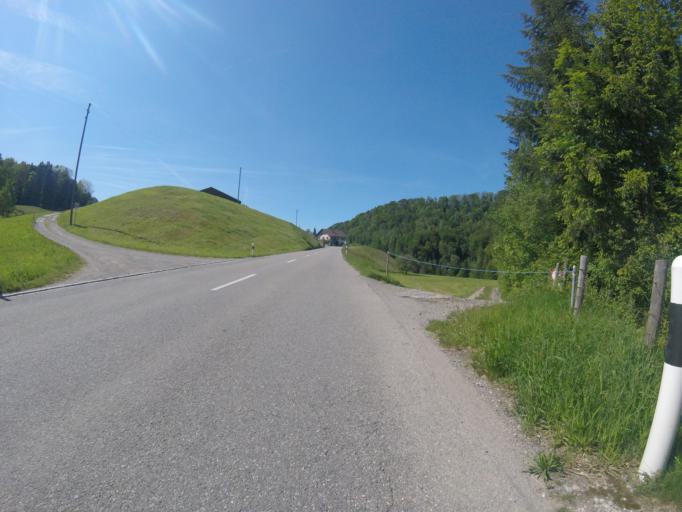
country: CH
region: Saint Gallen
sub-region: Wahlkreis Toggenburg
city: Ganterschwil
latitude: 47.3800
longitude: 9.1129
